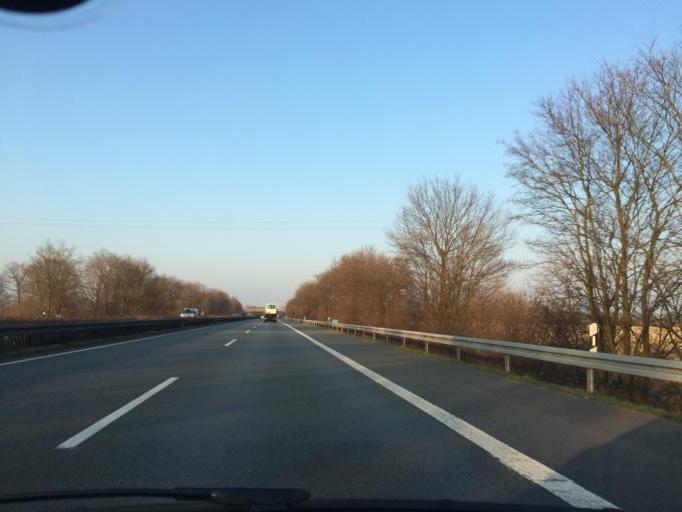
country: DE
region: North Rhine-Westphalia
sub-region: Regierungsbezirk Munster
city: Nottuln
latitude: 51.8963
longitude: 7.3798
